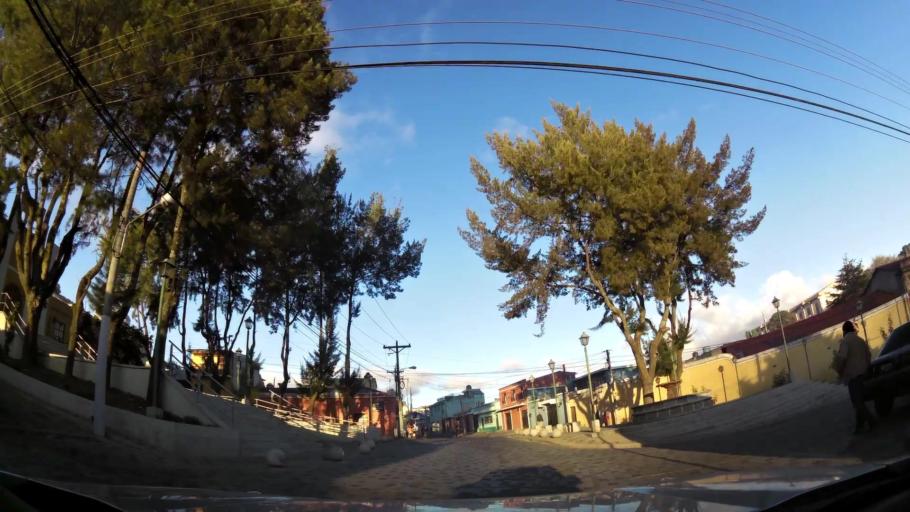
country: GT
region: Quetzaltenango
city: Quetzaltenango
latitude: 14.8314
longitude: -91.5201
